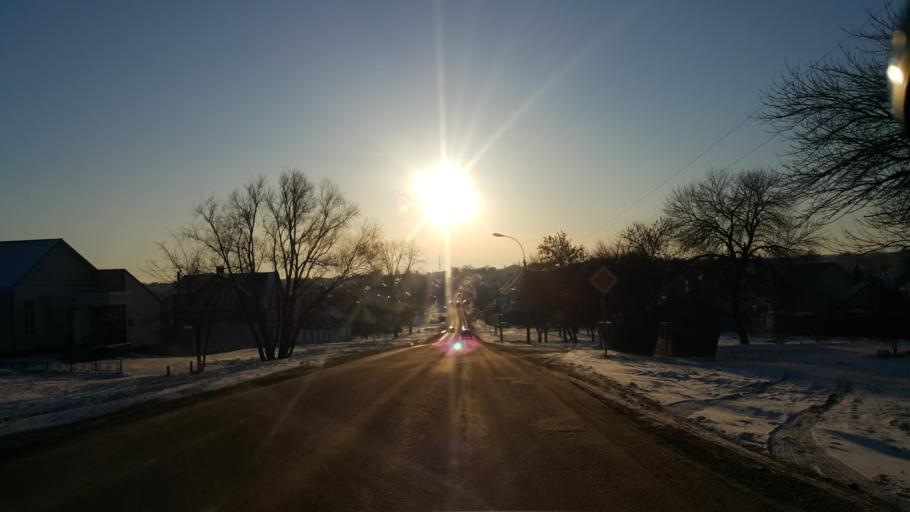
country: RU
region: Tambov
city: Pokrovo-Prigorodnoye
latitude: 52.7056
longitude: 41.4115
